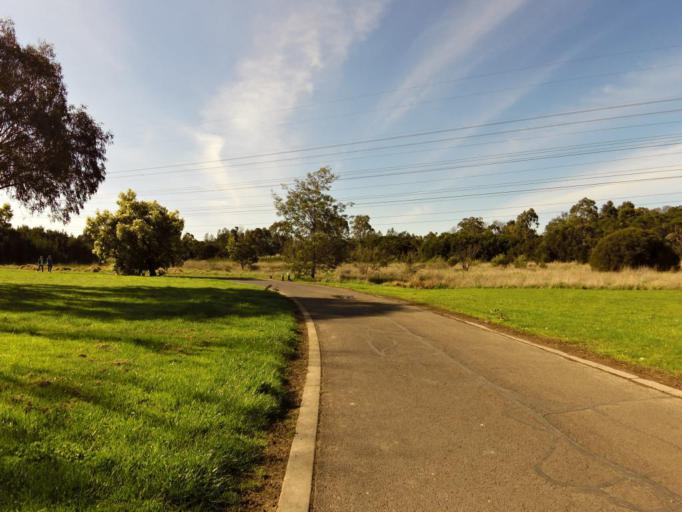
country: AU
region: Victoria
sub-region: Monash
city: Mulgrave
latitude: -37.9037
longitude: 145.2018
